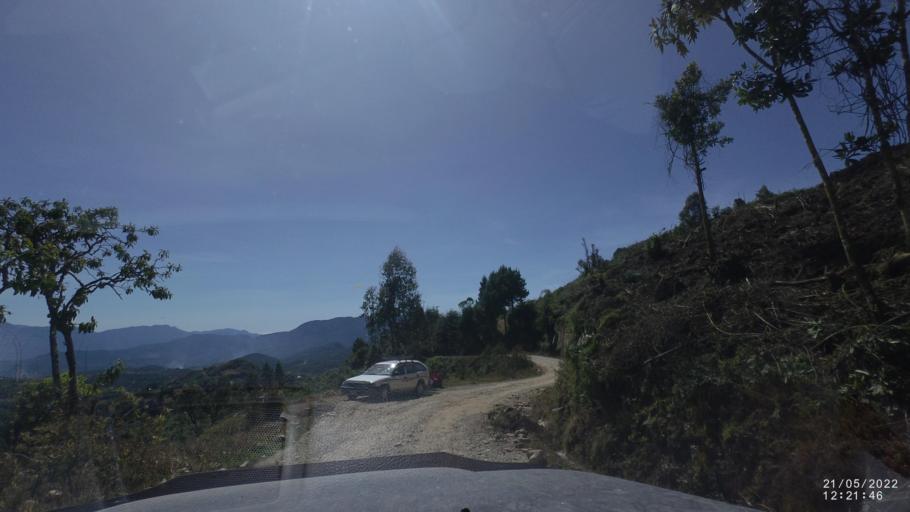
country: BO
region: Cochabamba
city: Colomi
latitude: -17.2241
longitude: -65.9039
